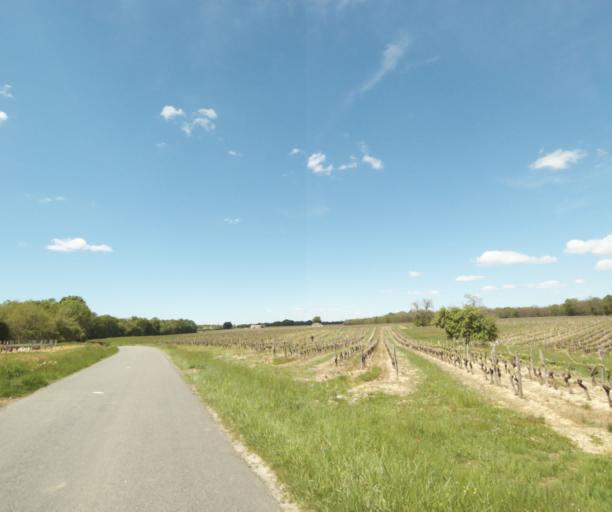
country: FR
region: Poitou-Charentes
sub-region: Departement de la Charente-Maritime
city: Burie
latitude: 45.7497
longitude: -0.4543
